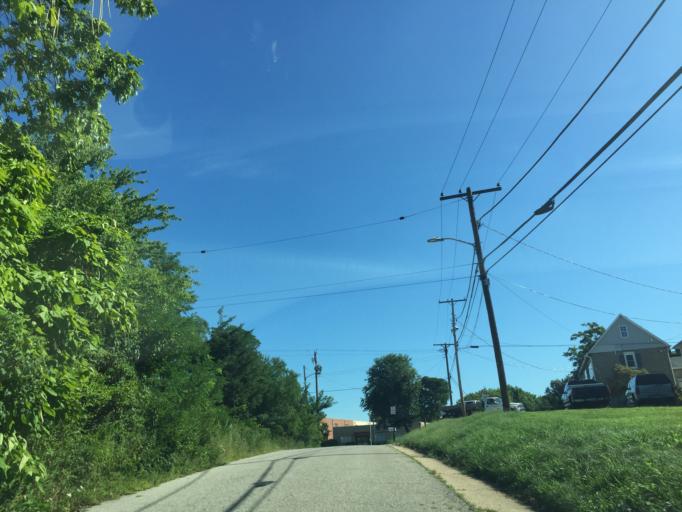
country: US
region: Maryland
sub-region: Baltimore County
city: Rosedale
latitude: 39.3094
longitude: -76.5355
